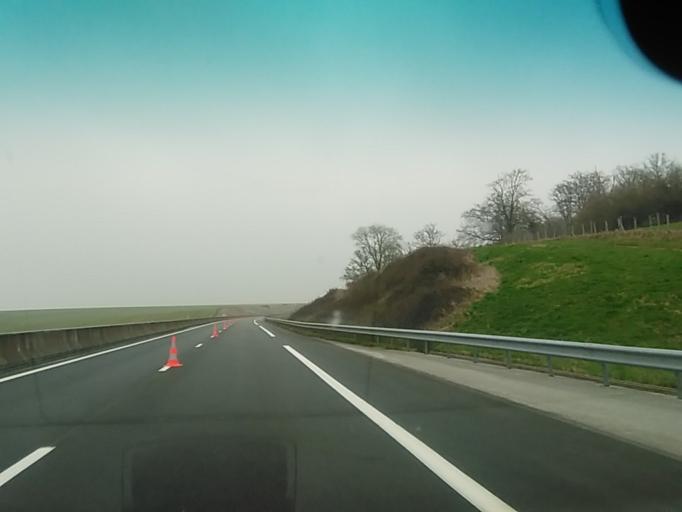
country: FR
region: Lower Normandy
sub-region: Departement de l'Orne
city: Sees
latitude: 48.6920
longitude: 0.2377
